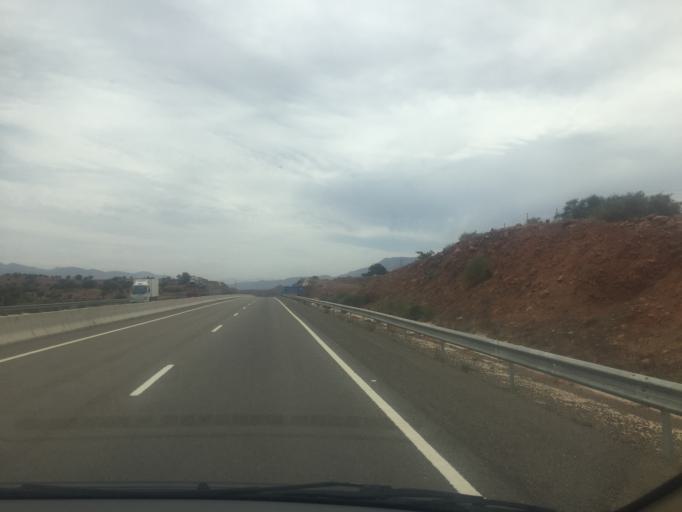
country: MA
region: Marrakech-Tensift-Al Haouz
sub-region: Chichaoua
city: Timezgadiouine
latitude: 30.8721
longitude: -9.0858
